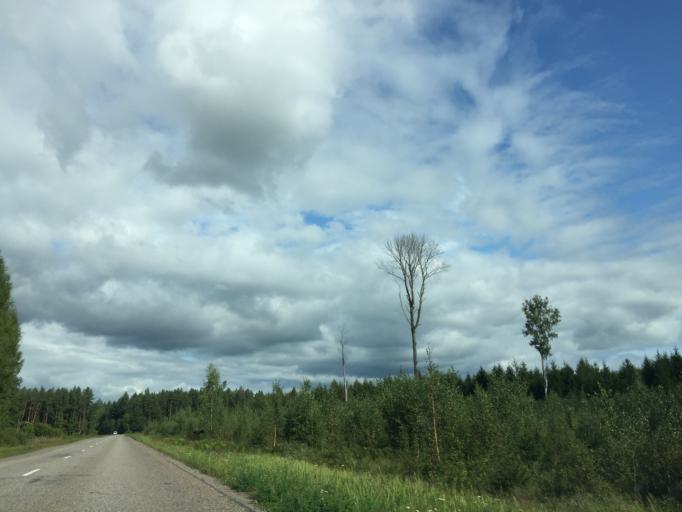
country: LV
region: Pargaujas
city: Stalbe
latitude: 57.4407
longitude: 24.9261
